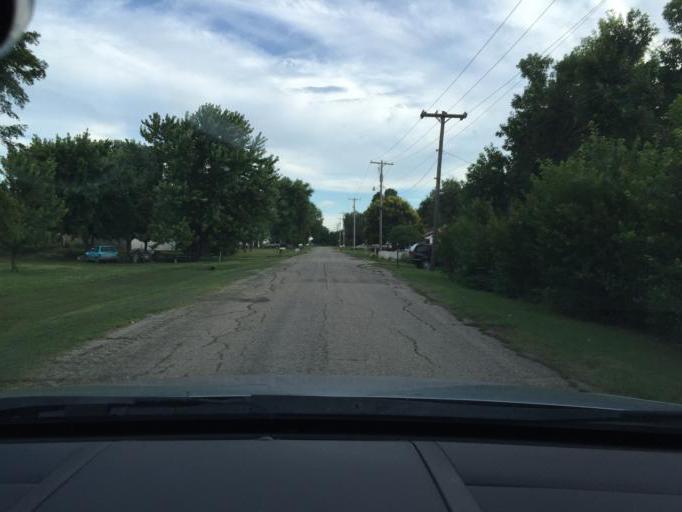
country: US
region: Kansas
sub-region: Reno County
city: Haven
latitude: 37.9285
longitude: -97.8868
